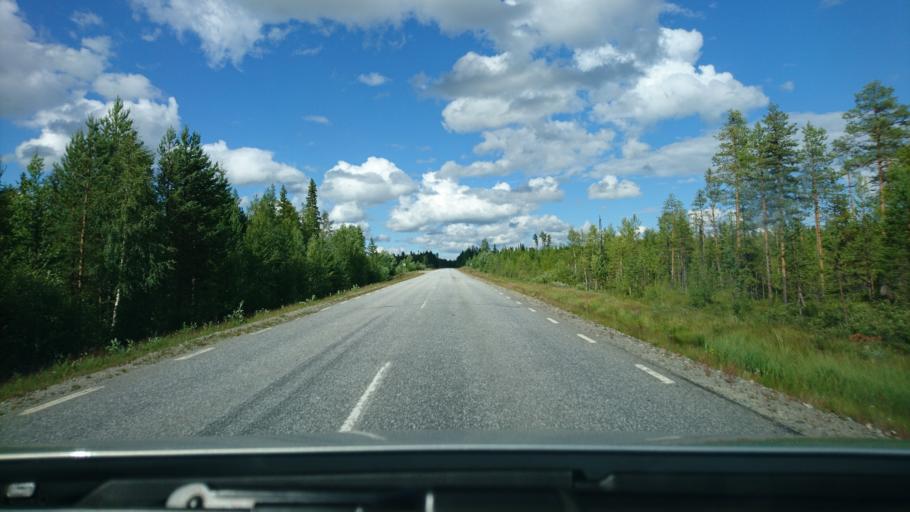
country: SE
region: Vaesterbotten
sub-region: Asele Kommun
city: Asele
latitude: 64.0631
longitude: 17.2809
